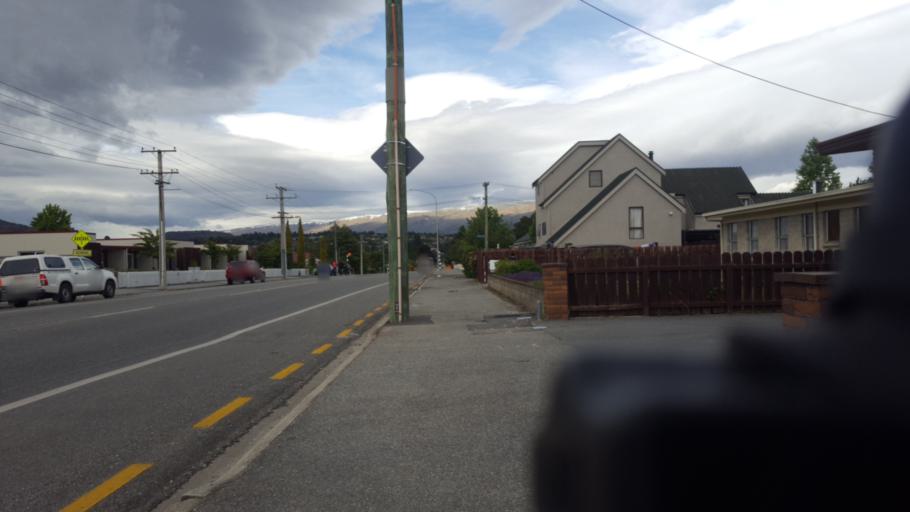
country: NZ
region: Otago
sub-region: Queenstown-Lakes District
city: Wanaka
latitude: -45.2493
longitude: 169.3981
